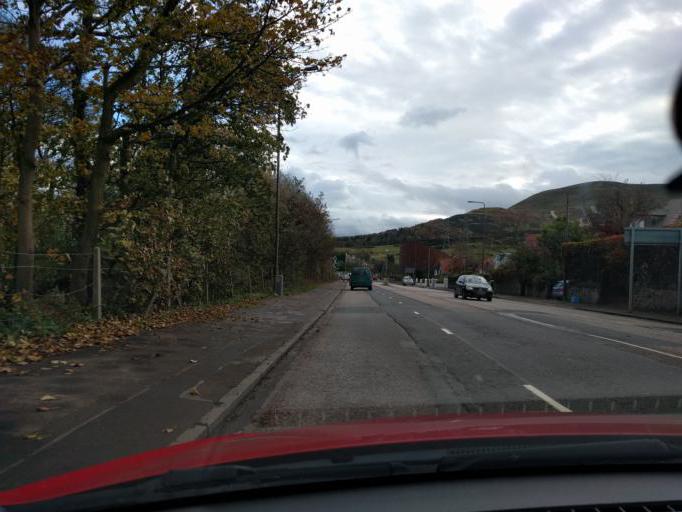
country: GB
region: Scotland
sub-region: Midlothian
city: Loanhead
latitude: 55.8992
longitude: -3.2040
